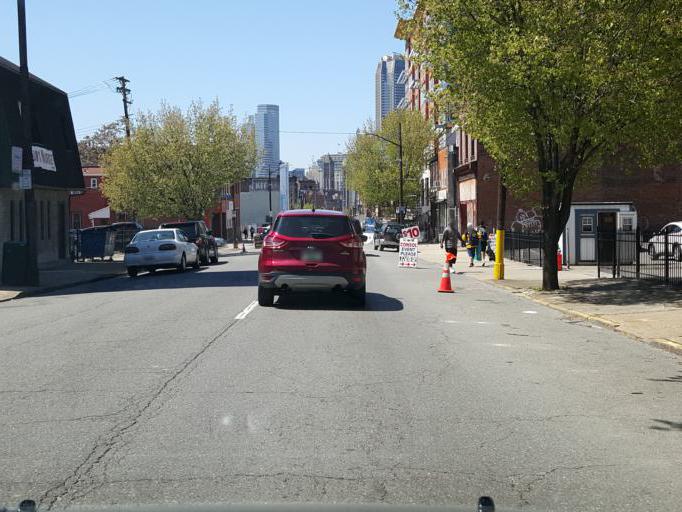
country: US
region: Pennsylvania
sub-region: Allegheny County
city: Pittsburgh
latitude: 40.4384
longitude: -79.9817
